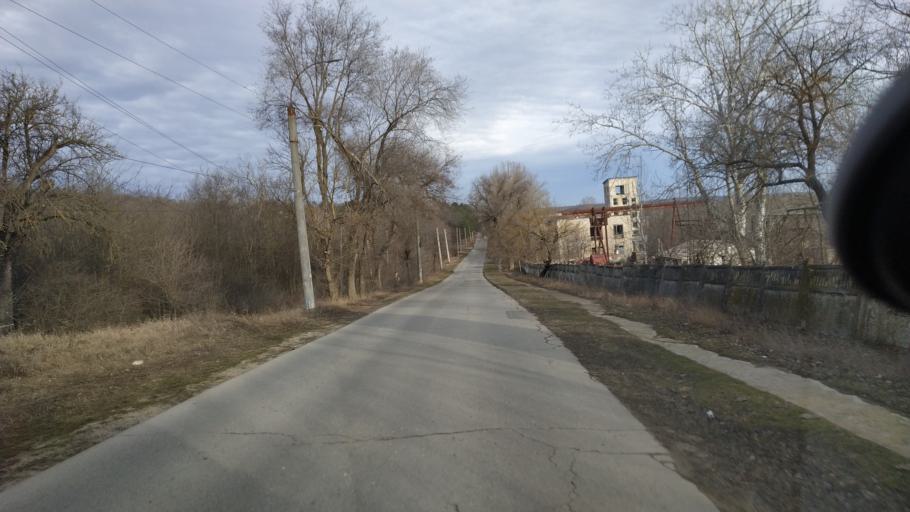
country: MD
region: Chisinau
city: Vadul lui Voda
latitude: 47.0989
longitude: 29.0693
